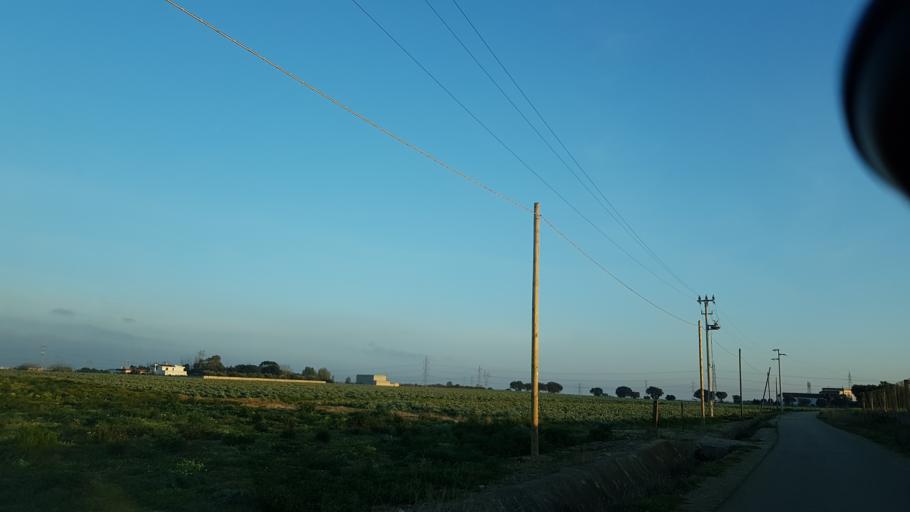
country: IT
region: Apulia
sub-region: Provincia di Brindisi
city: La Rosa
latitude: 40.6061
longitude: 17.9385
